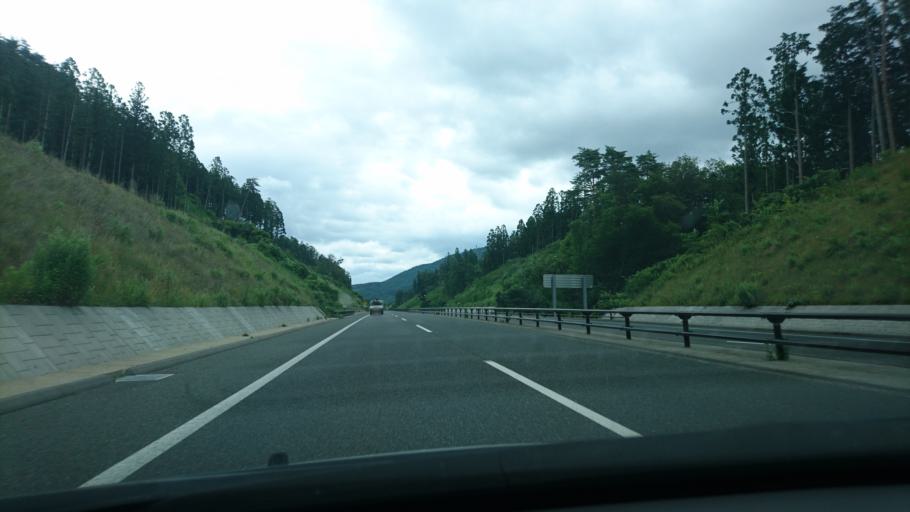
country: JP
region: Iwate
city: Ofunato
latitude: 39.0285
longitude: 141.6563
